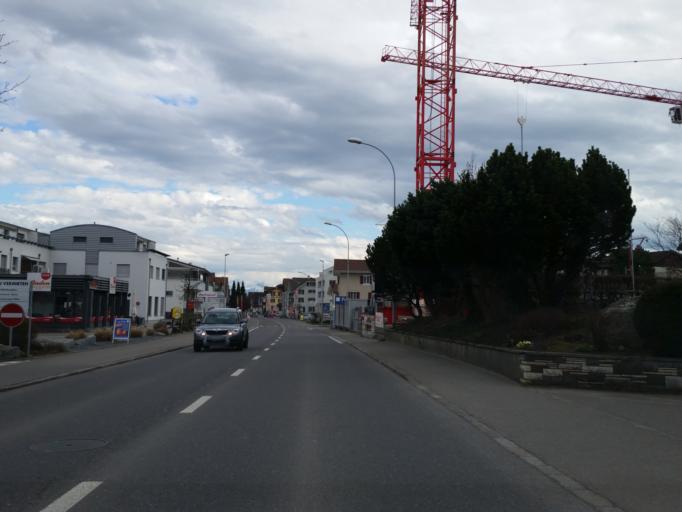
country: CH
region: Lucerne
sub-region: Sursee District
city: Nottwil
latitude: 47.1376
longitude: 8.1319
